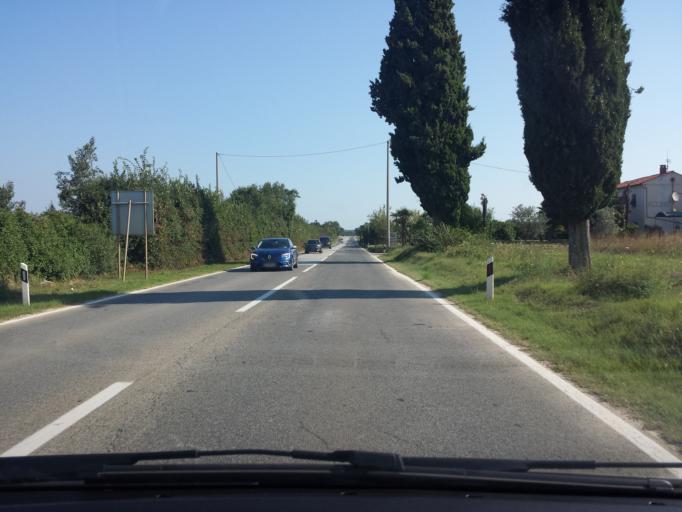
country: HR
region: Istarska
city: Galizana
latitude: 44.9113
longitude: 13.8485
